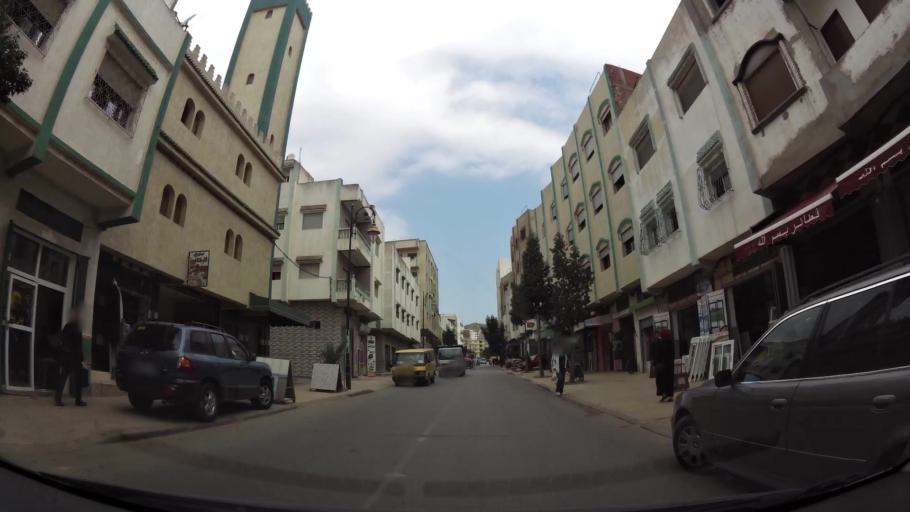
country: MA
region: Tanger-Tetouan
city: Tetouan
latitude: 35.5681
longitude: -5.3931
